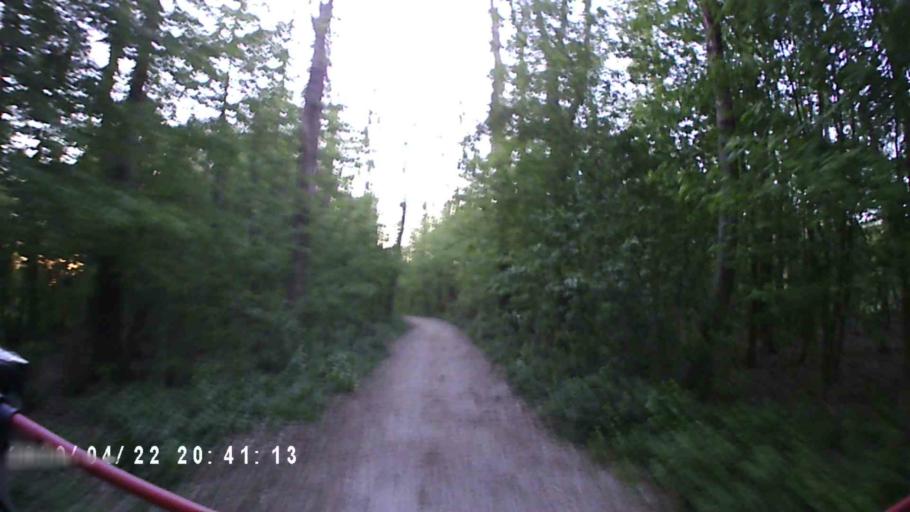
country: NL
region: Groningen
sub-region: Gemeente Winsum
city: Winsum
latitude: 53.3233
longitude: 6.5348
